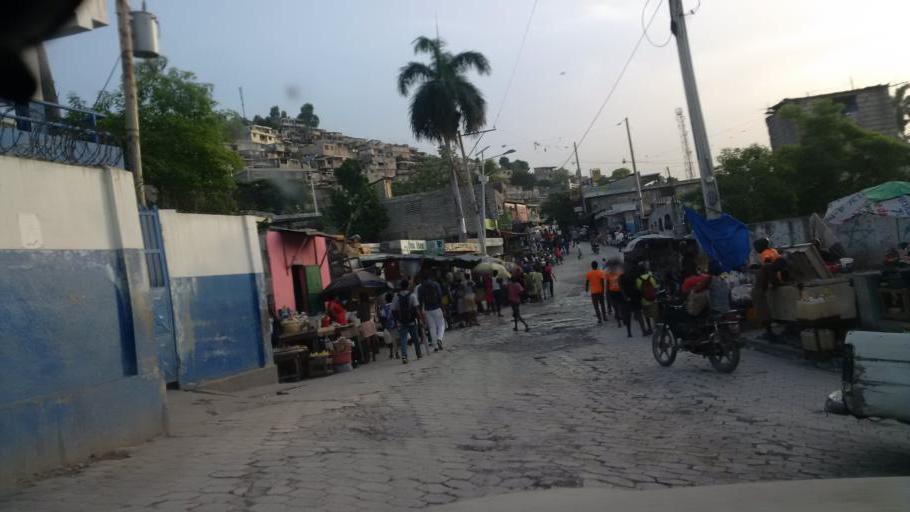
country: HT
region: Ouest
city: Port-au-Prince
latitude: 18.5264
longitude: -72.3560
